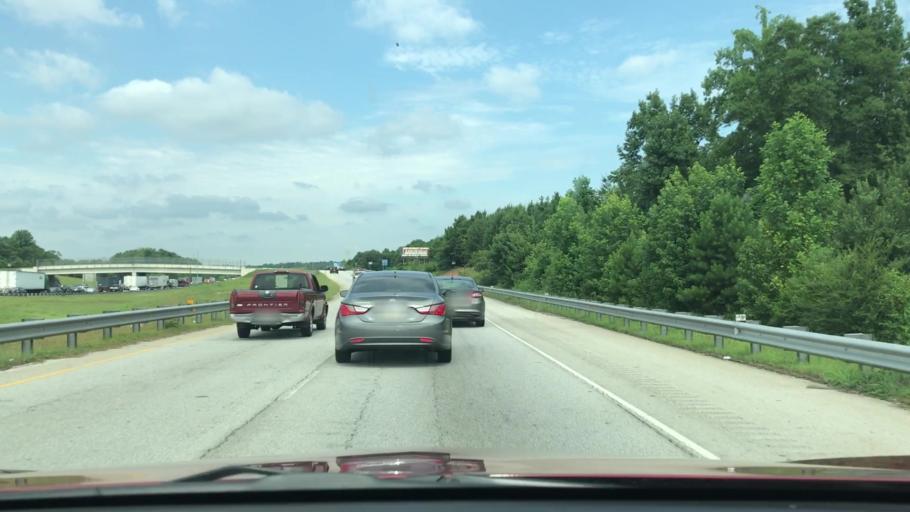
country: US
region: Georgia
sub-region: DeKalb County
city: Lithonia
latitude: 33.7024
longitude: -84.1204
